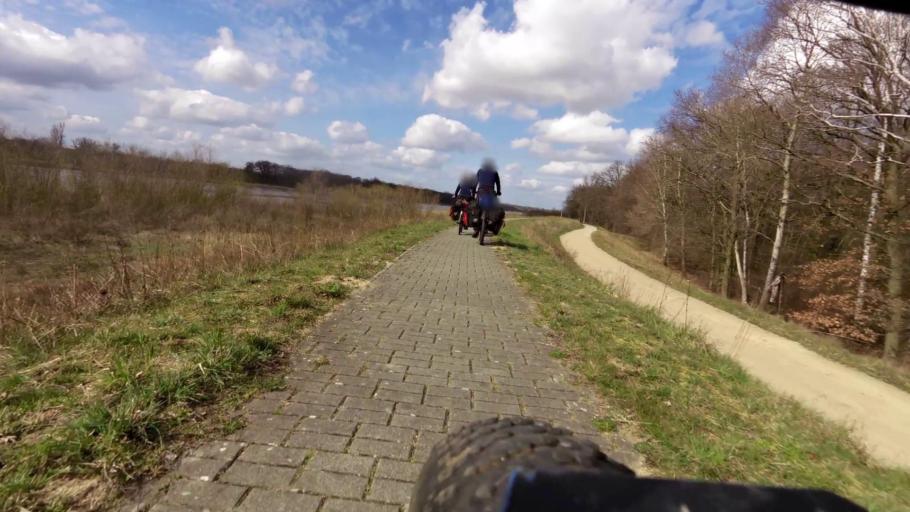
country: PL
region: Lubusz
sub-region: Powiat slubicki
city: Slubice
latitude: 52.3818
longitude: 14.5499
